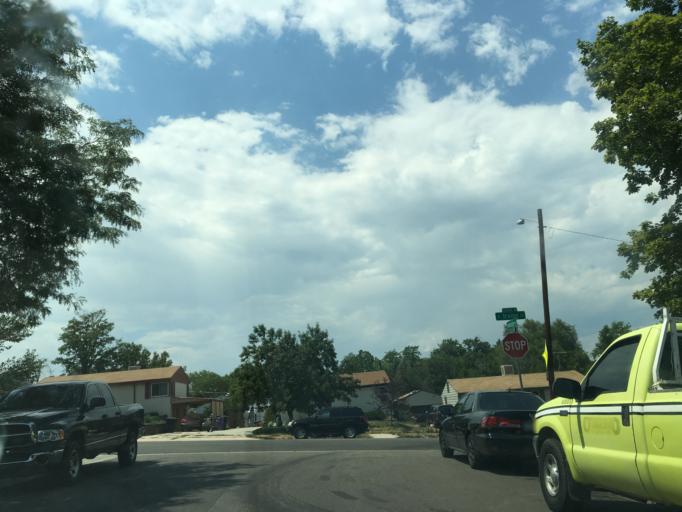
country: US
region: Colorado
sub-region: Arapahoe County
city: Sheridan
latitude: 39.6859
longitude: -105.0294
